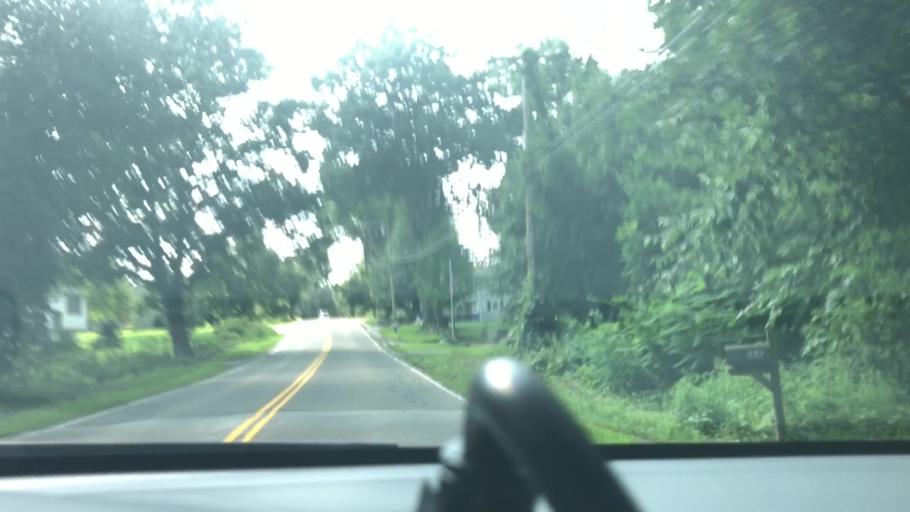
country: US
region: New Hampshire
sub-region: Hillsborough County
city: Pinardville
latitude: 42.9896
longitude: -71.5184
